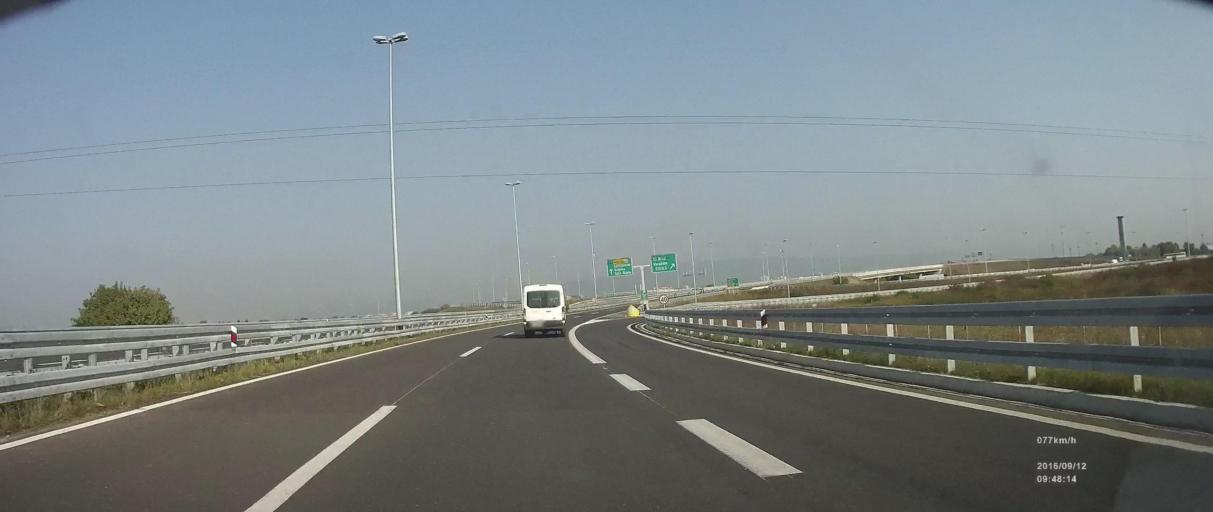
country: HR
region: Grad Zagreb
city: Odra
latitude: 45.7479
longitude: 16.0049
